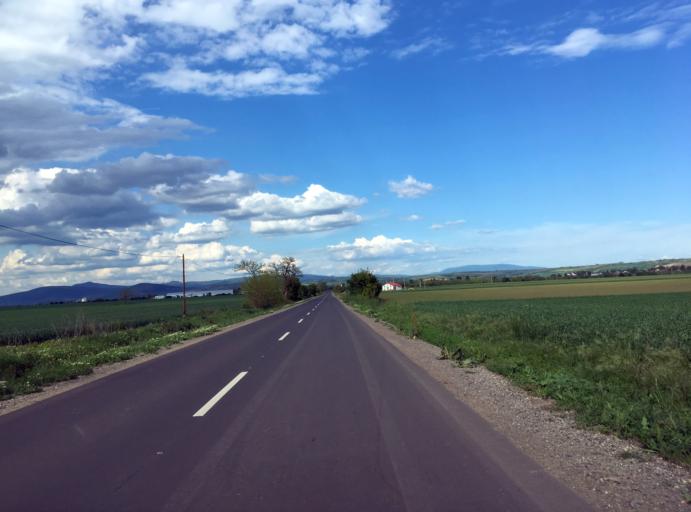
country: HU
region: Heves
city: Hered
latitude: 47.7180
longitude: 19.6463
